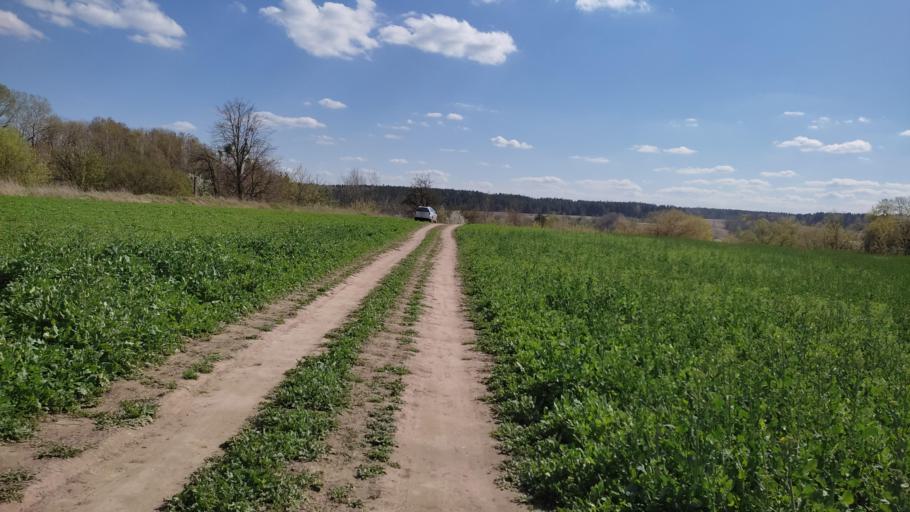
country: BY
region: Grodnenskaya
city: Hrodna
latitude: 53.6549
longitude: 23.9057
